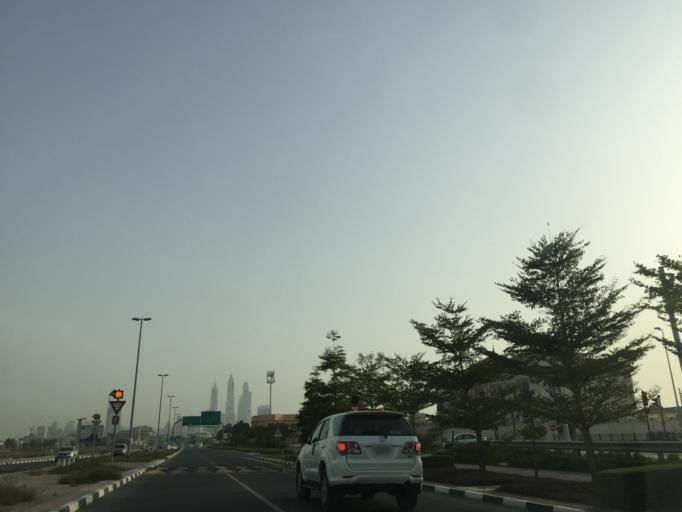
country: AE
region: Dubai
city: Dubai
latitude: 25.1146
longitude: 55.1763
